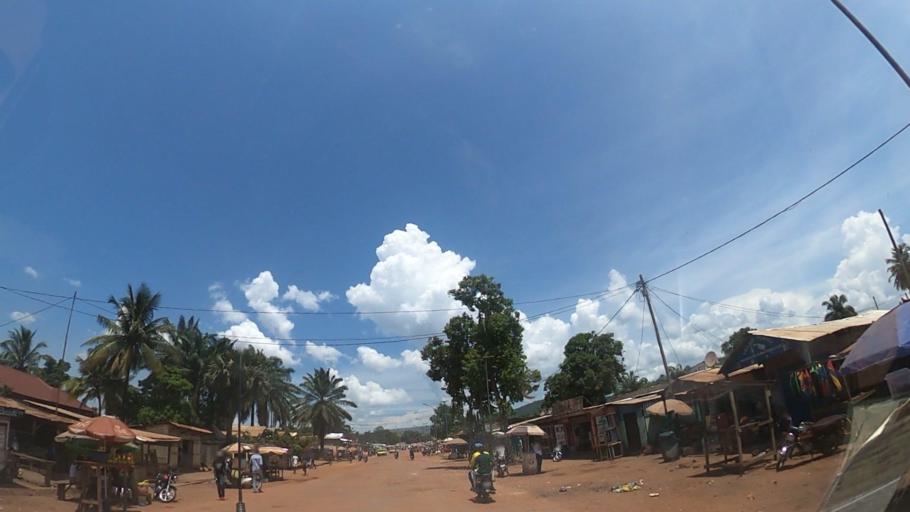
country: CF
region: Bangui
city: Bangui
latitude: 4.3615
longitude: 18.5609
